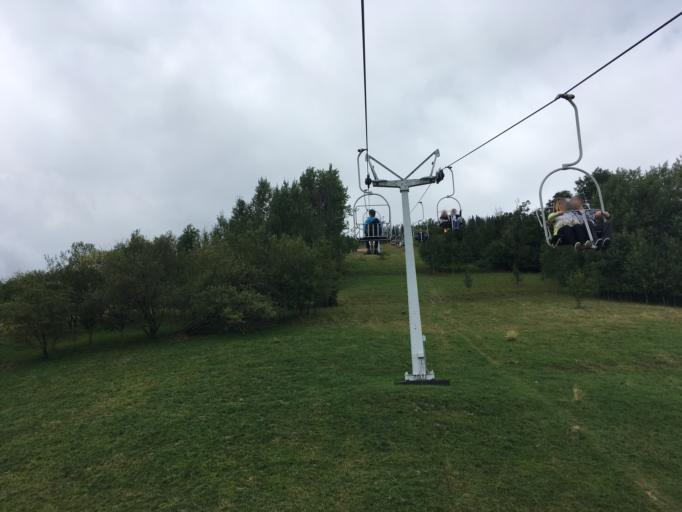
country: PL
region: Lesser Poland Voivodeship
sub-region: Powiat tatrzanski
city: Koscielisko
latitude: 49.2961
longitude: 19.9133
